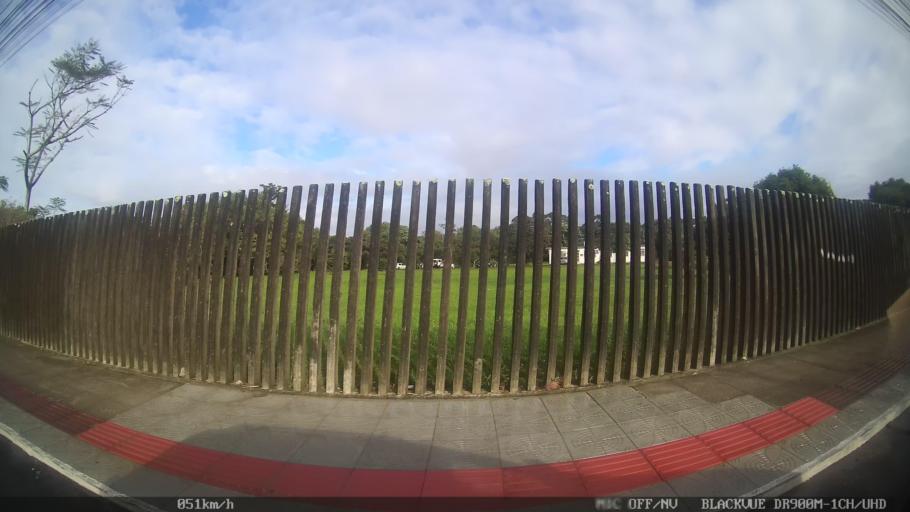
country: BR
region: Santa Catarina
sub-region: Sao Jose
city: Campinas
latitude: -27.6005
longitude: -48.6211
